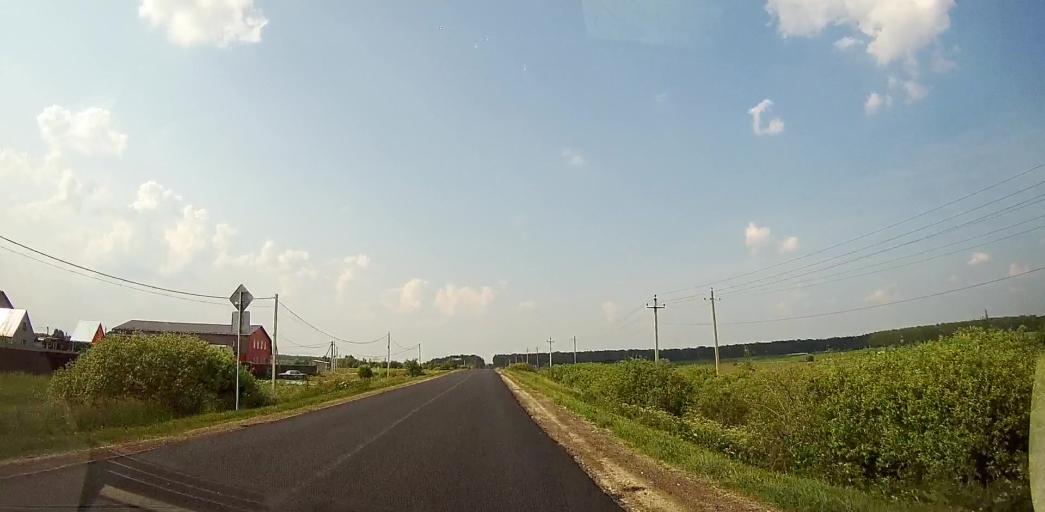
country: RU
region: Moskovskaya
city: Il'inskoye
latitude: 55.2234
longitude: 37.9263
